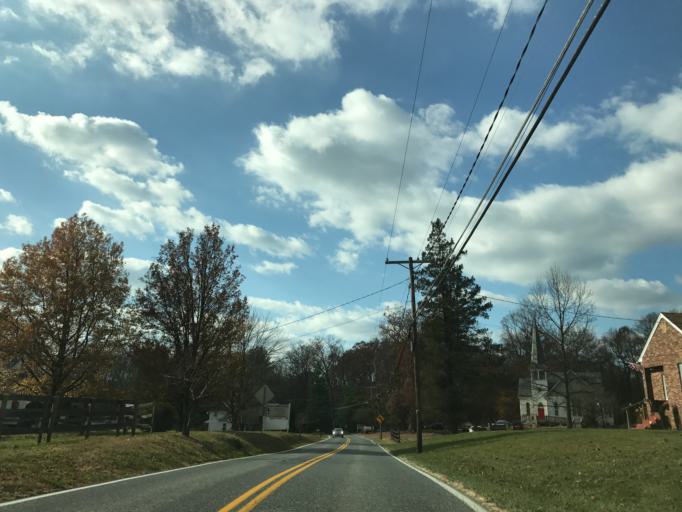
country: US
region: Maryland
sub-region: Harford County
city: Pleasant Hills
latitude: 39.4793
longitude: -76.3763
